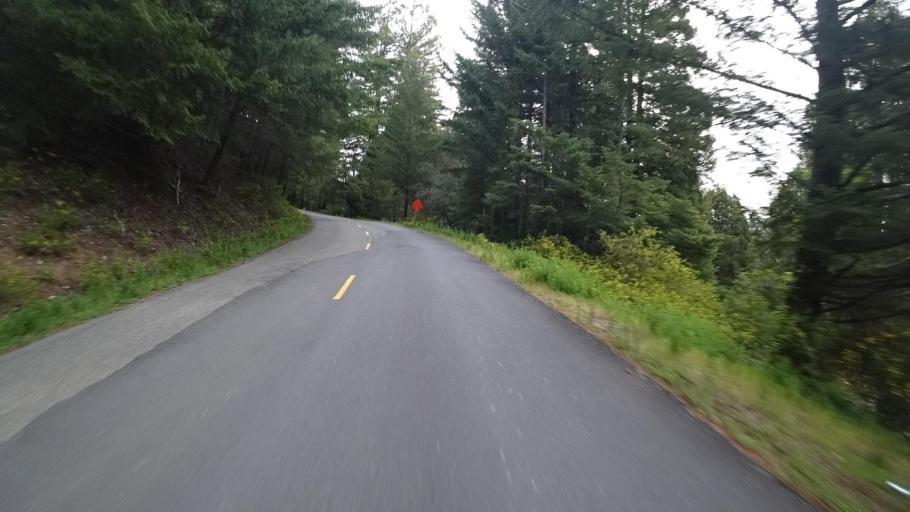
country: US
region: California
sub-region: Humboldt County
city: Redway
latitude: 40.2849
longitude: -123.8371
